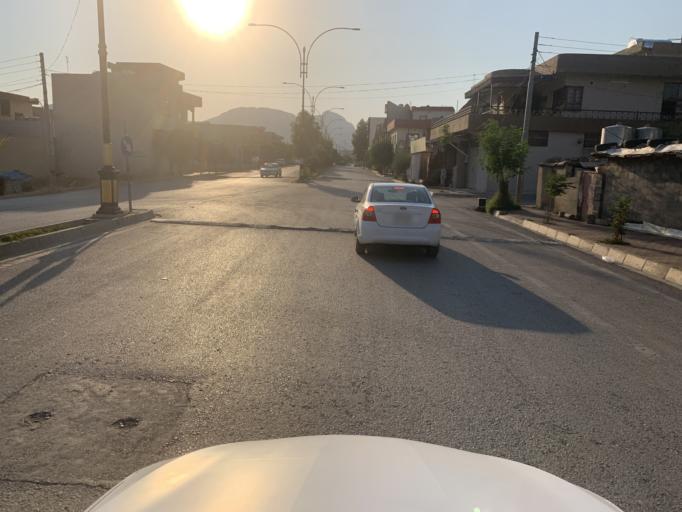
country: IQ
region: As Sulaymaniyah
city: Raniye
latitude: 36.2387
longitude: 44.8794
